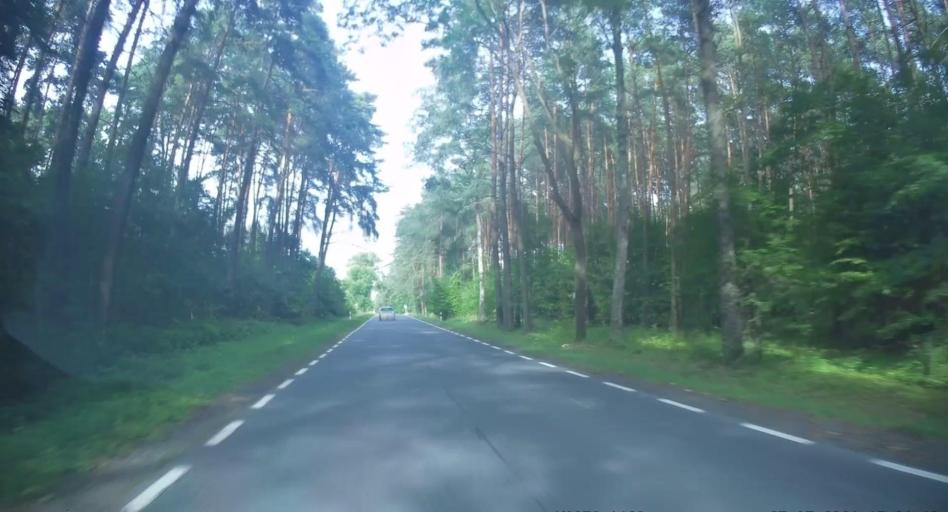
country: PL
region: Lodz Voivodeship
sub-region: Powiat tomaszowski
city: Inowlodz
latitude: 51.5492
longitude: 20.2438
